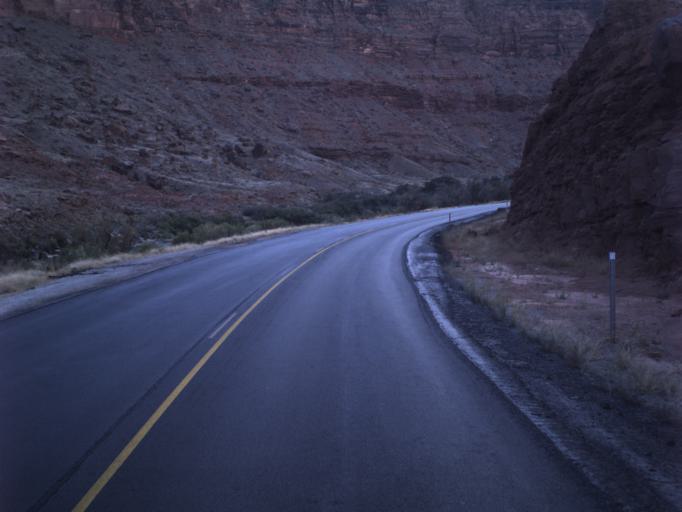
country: US
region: Utah
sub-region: Grand County
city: Moab
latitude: 38.6460
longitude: -109.4954
